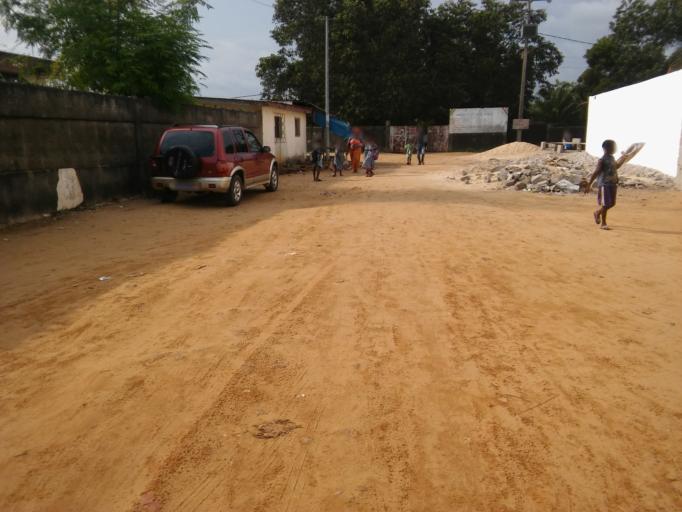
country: CI
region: Sud-Comoe
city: Grand-Bassam
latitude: 5.2186
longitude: -3.7312
